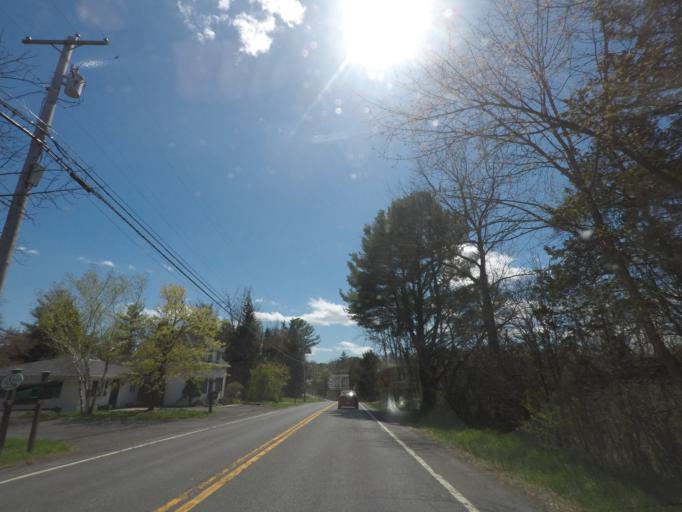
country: US
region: New York
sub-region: Greene County
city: Catskill
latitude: 42.2400
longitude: -73.8539
